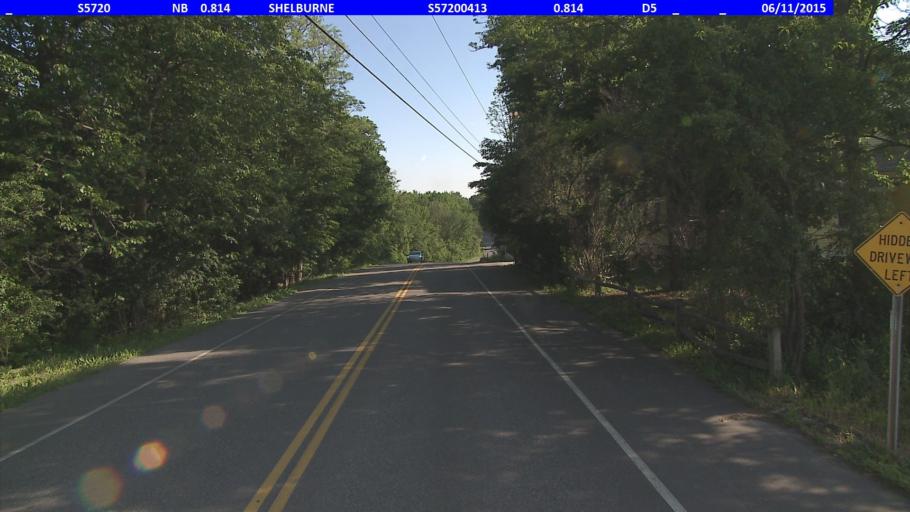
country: US
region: Vermont
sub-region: Chittenden County
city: South Burlington
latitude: 44.3798
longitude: -73.2021
